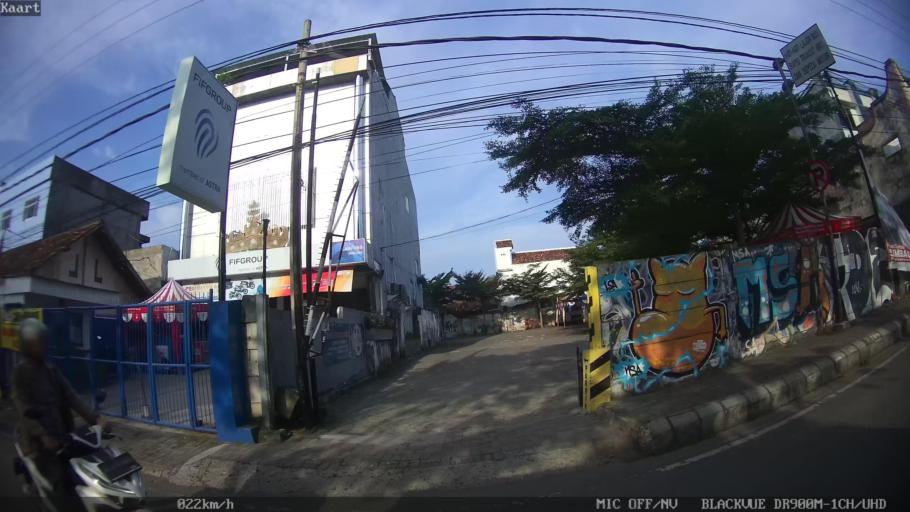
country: ID
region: Lampung
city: Kedaton
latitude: -5.3885
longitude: 105.2619
